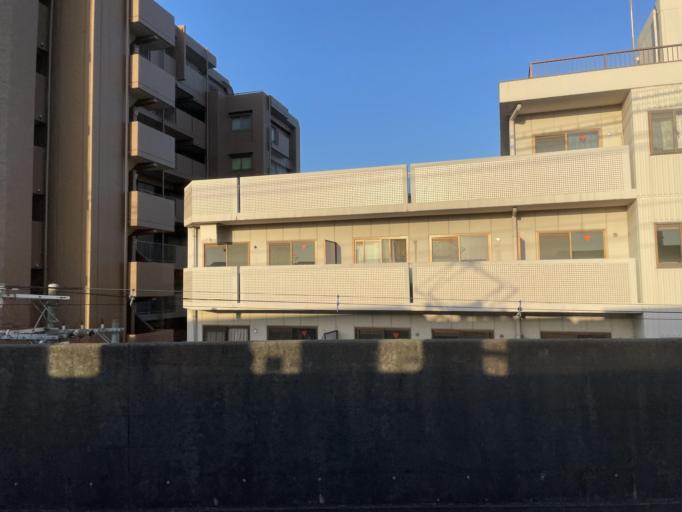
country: JP
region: Osaka
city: Osaka-shi
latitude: 34.6353
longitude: 135.5278
